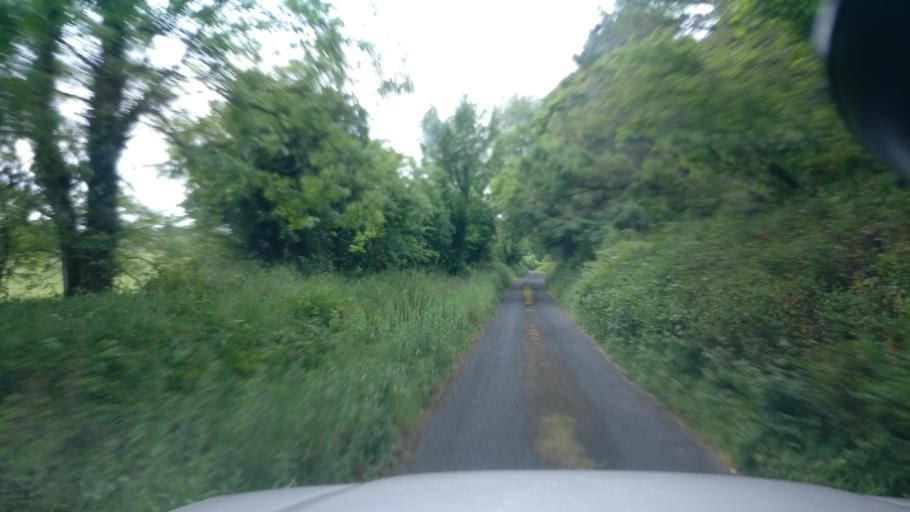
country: IE
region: Connaught
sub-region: County Galway
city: Ballinasloe
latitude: 53.2721
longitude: -8.3621
